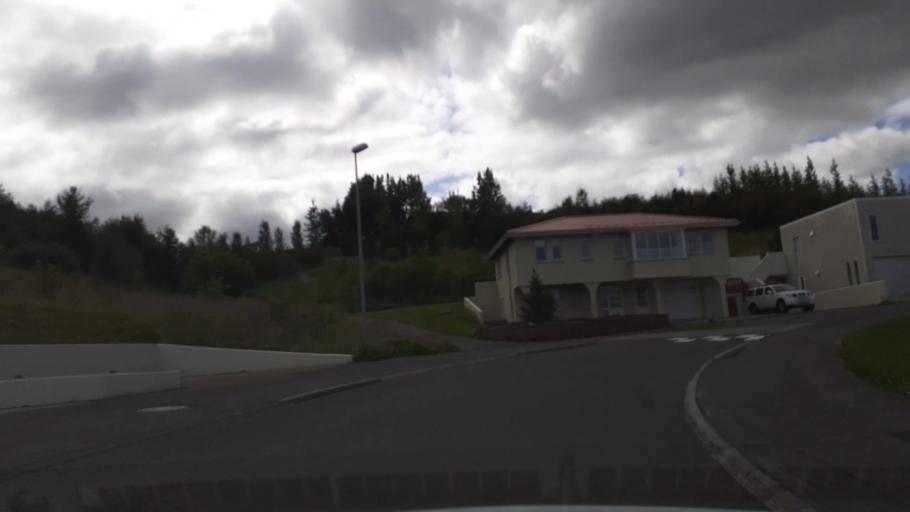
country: IS
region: Northeast
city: Akureyri
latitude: 65.6848
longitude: -18.1098
